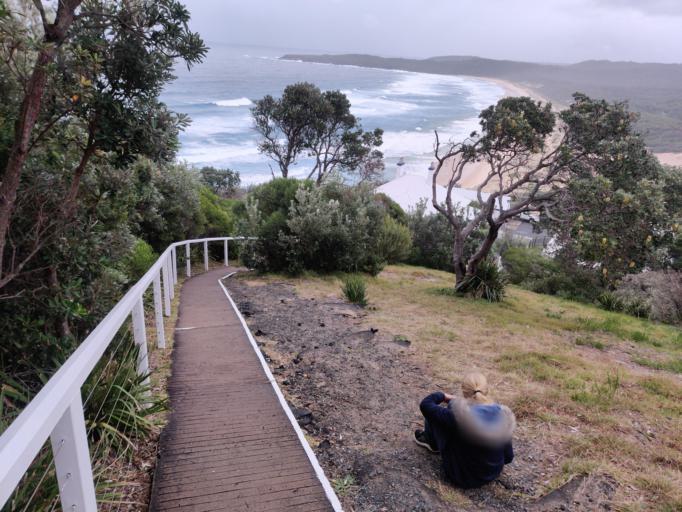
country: AU
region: New South Wales
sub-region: Great Lakes
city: Forster
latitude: -32.4411
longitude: 152.5390
